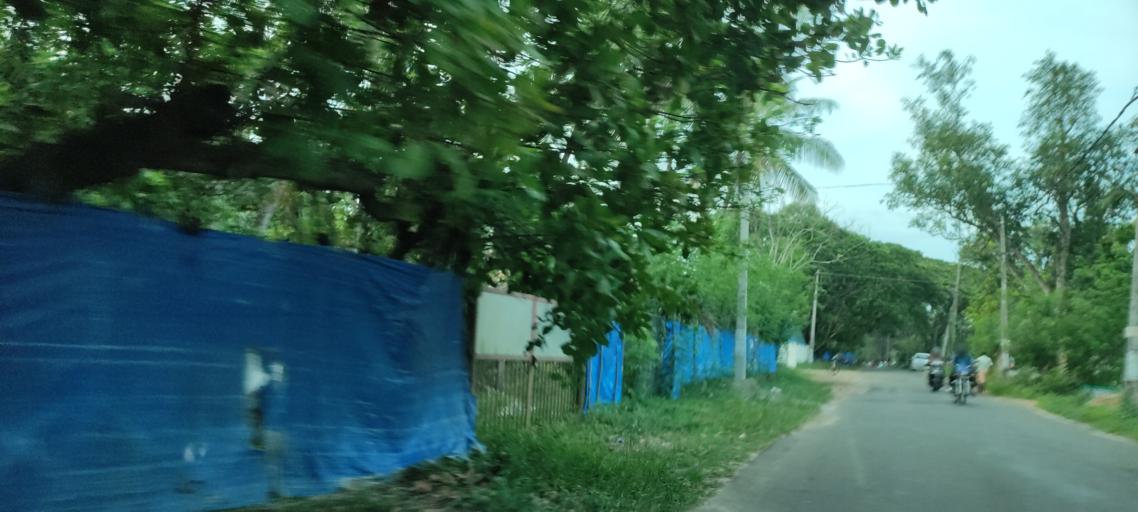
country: IN
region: Kerala
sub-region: Alappuzha
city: Shertallai
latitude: 9.7010
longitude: 76.3560
